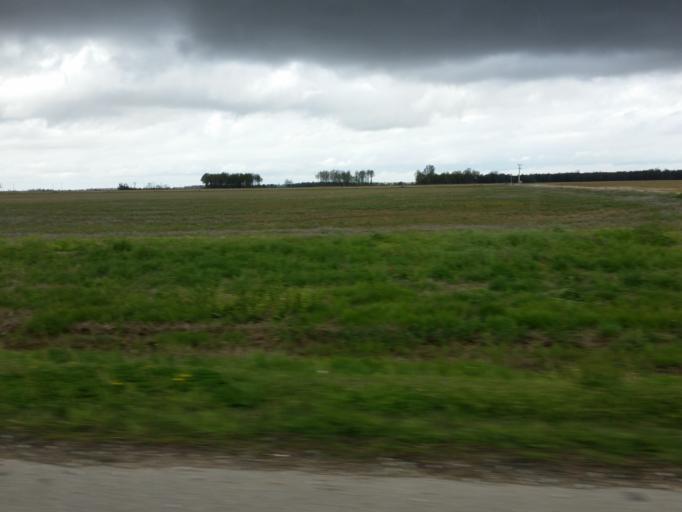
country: US
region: Arkansas
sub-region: Clay County
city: Corning
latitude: 36.5027
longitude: -90.5399
